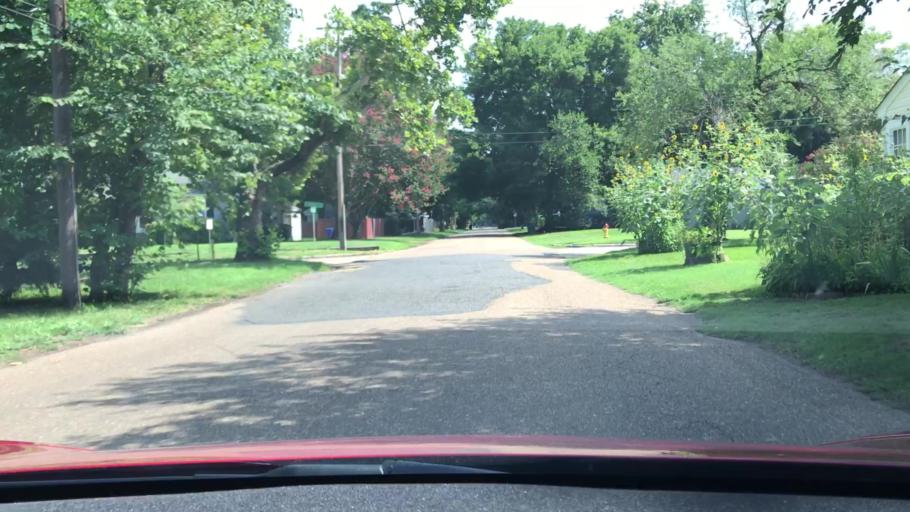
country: US
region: Louisiana
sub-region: Bossier Parish
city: Bossier City
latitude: 32.4748
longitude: -93.7313
